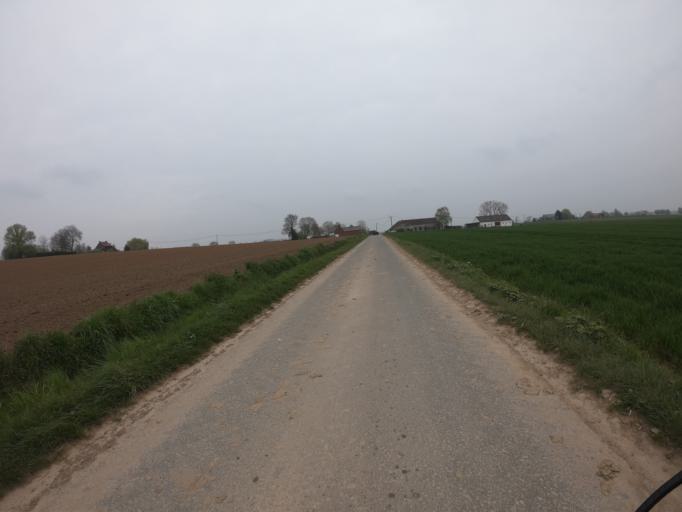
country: BE
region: Wallonia
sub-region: Province du Hainaut
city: Flobecq
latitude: 50.7569
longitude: 3.7781
